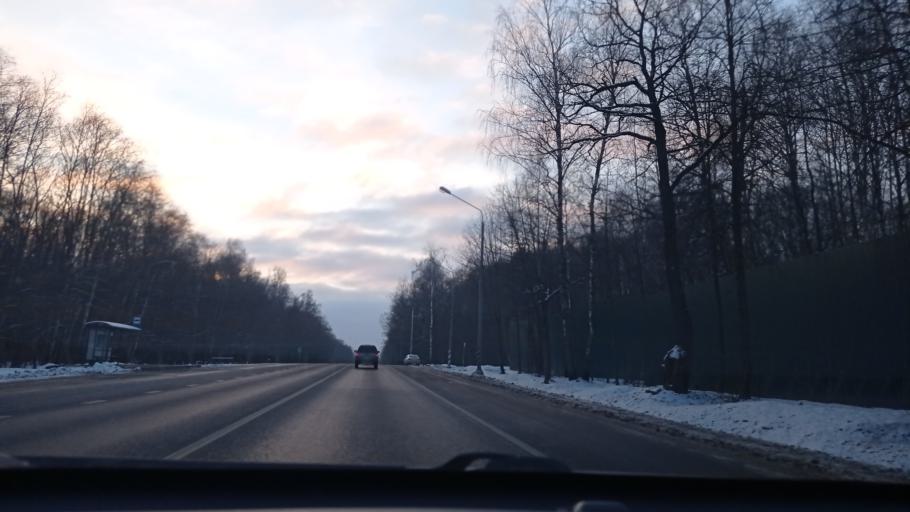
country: RU
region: Moskovskaya
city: Selyatino
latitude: 55.2682
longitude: 37.1195
